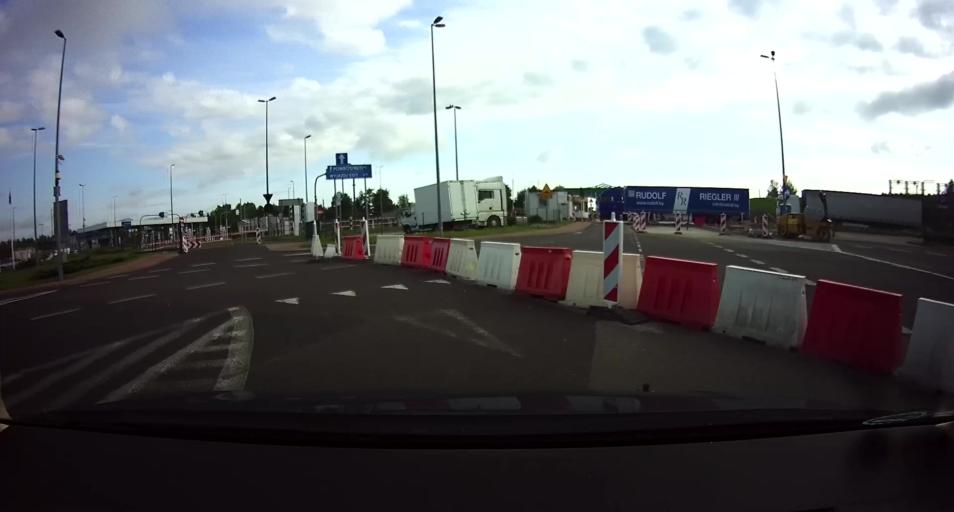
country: PL
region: Podlasie
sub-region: Powiat sokolski
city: Kuznica
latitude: 53.5211
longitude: 23.6585
